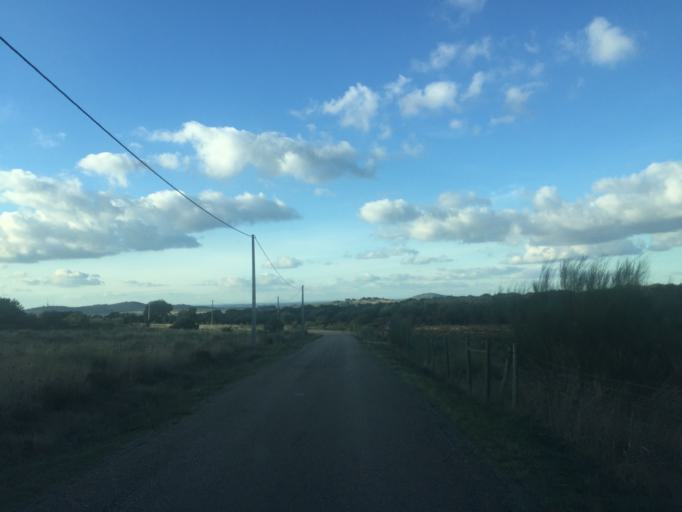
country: PT
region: Portalegre
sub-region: Alter do Chao
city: Alter do Chao
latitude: 39.1892
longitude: -7.6296
